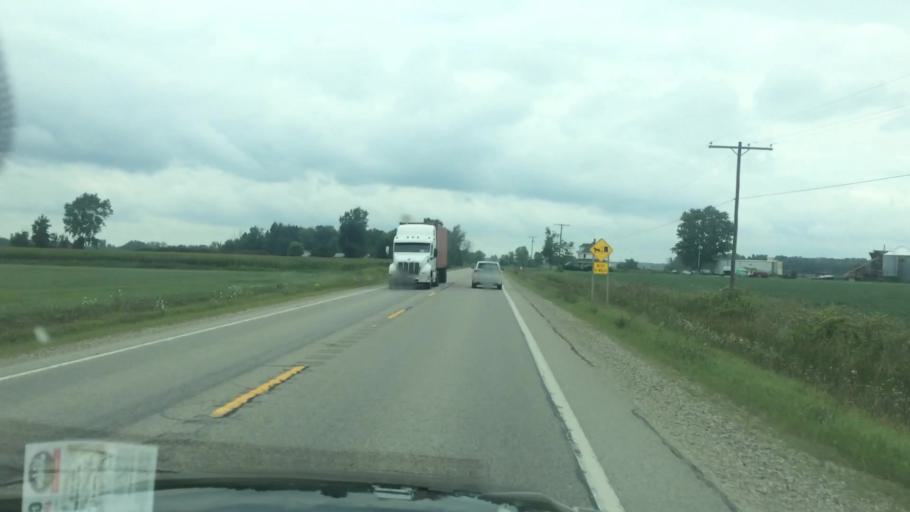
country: US
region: Michigan
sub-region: Tuscola County
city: Cass City
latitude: 43.5169
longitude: -83.0926
